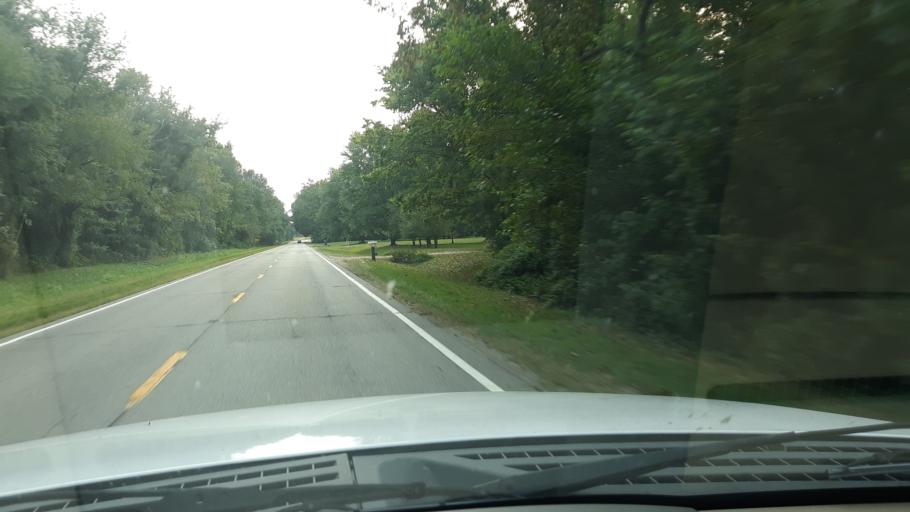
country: US
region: Illinois
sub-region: Edwards County
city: Grayville
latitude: 38.3171
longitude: -87.9274
